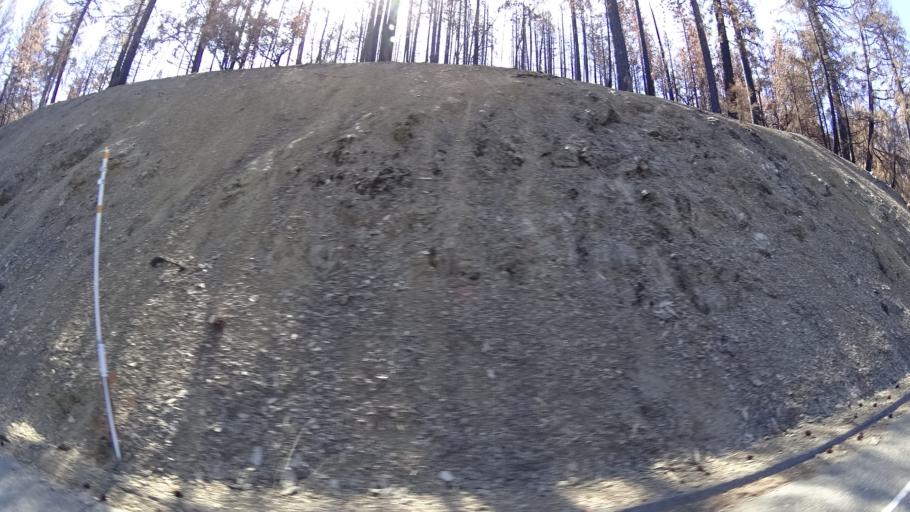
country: US
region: California
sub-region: Tehama County
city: Rancho Tehama Reserve
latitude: 39.6646
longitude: -122.7165
